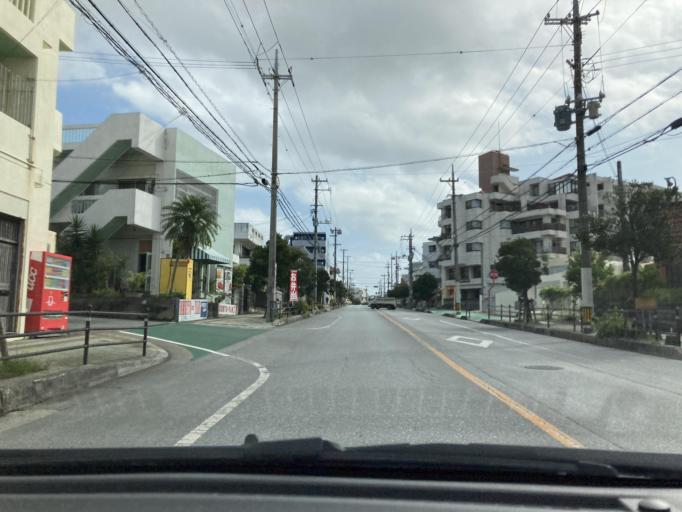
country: JP
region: Okinawa
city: Ginowan
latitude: 26.2622
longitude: 127.7573
